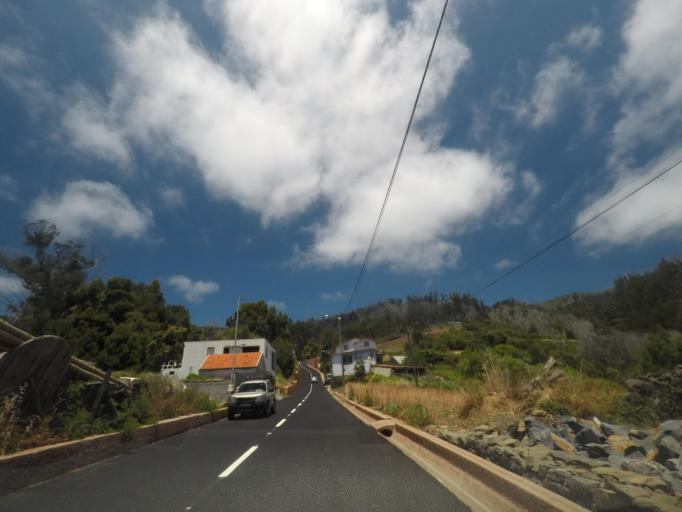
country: PT
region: Madeira
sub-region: Calheta
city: Estreito da Calheta
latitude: 32.7388
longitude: -17.1649
